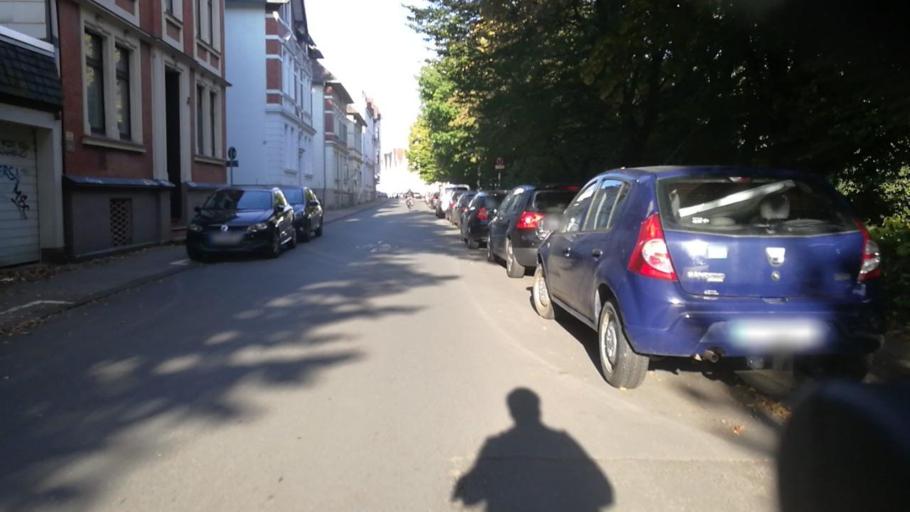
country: DE
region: North Rhine-Westphalia
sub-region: Regierungsbezirk Detmold
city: Bielefeld
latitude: 52.0129
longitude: 8.5436
